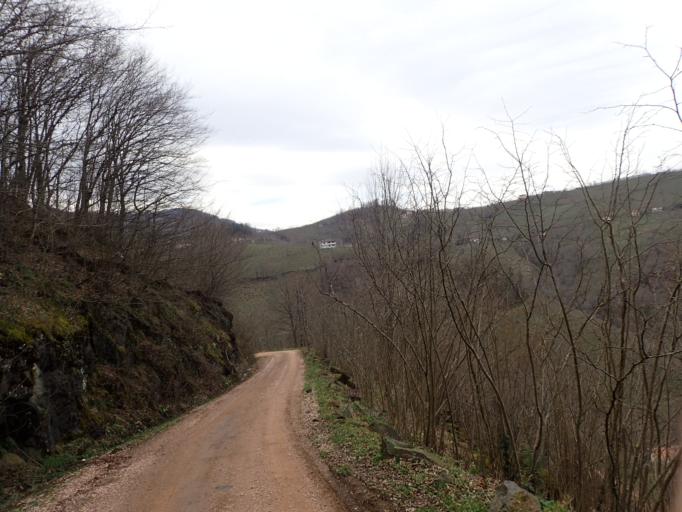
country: TR
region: Ordu
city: Camas
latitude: 40.8914
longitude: 37.5058
